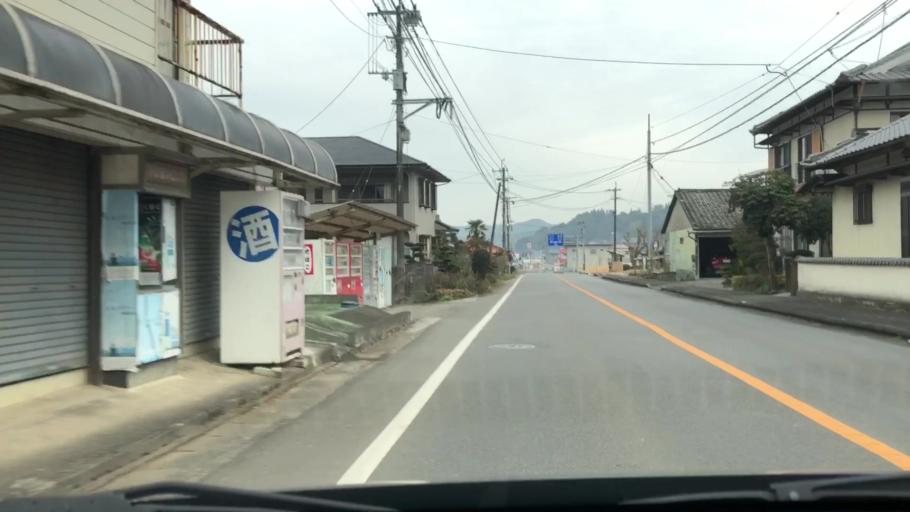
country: JP
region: Oita
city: Usuki
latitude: 33.0301
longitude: 131.6880
